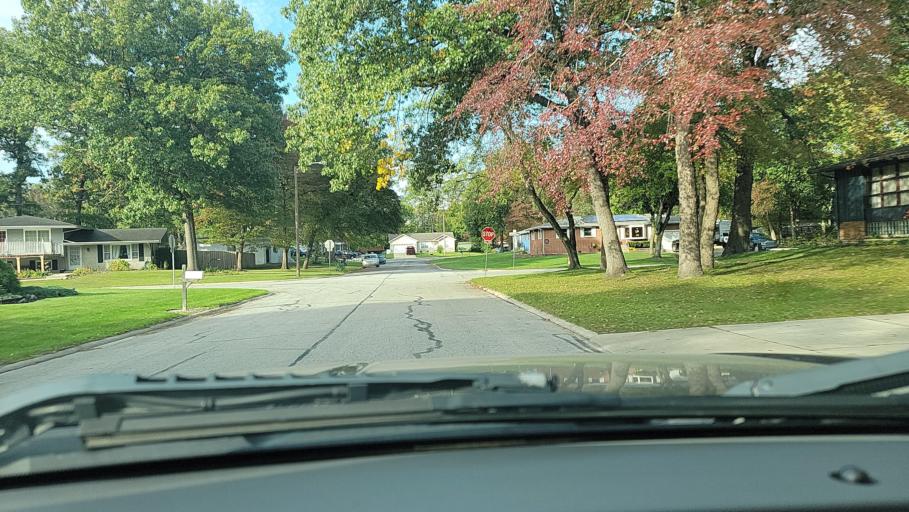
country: US
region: Indiana
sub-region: Porter County
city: Portage
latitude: 41.5837
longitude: -87.1729
